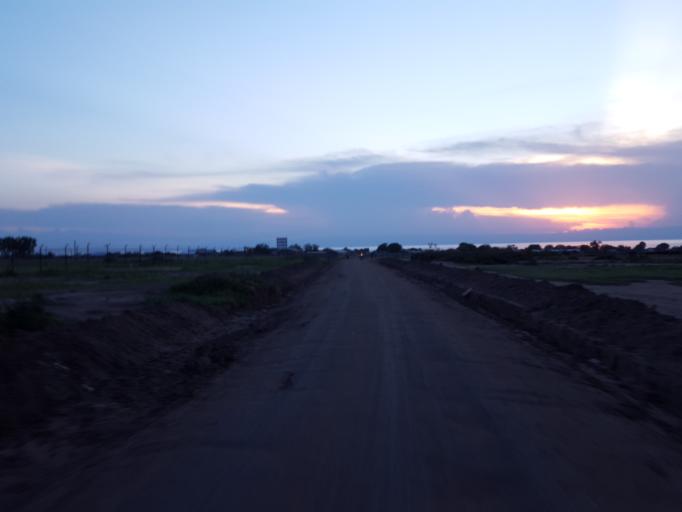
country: UG
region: Western Region
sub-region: Kibale District
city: Kagadi
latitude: 1.2379
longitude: 30.7422
